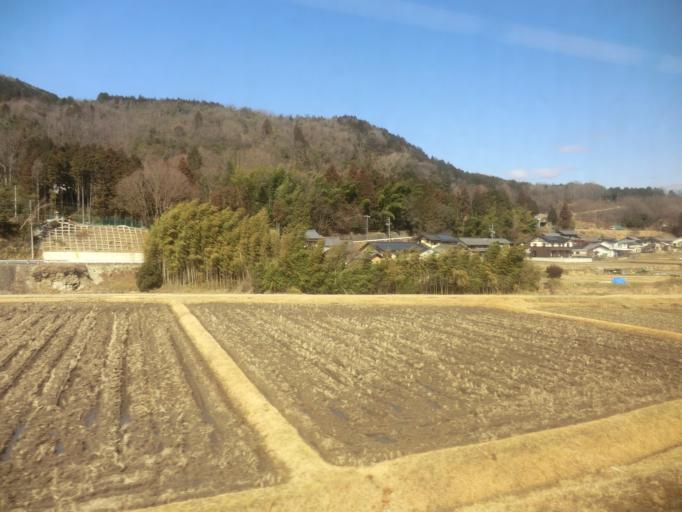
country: JP
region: Gifu
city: Mizunami
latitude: 35.4241
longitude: 137.3294
